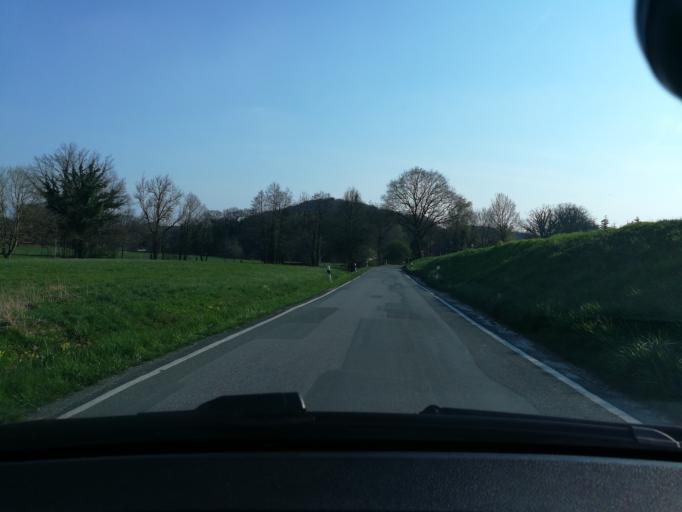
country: DE
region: North Rhine-Westphalia
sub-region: Regierungsbezirk Detmold
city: Werther
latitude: 52.0403
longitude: 8.4124
